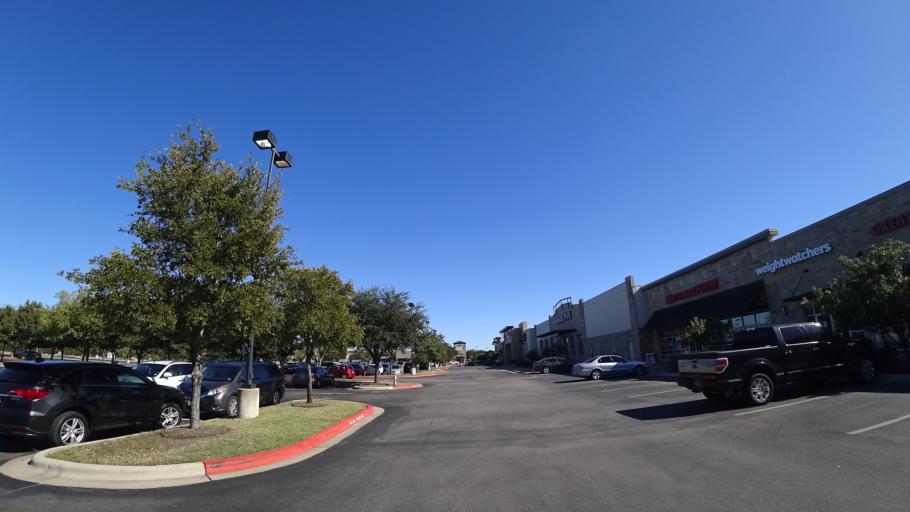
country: US
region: Texas
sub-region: Travis County
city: Rollingwood
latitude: 30.2310
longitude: -97.8172
